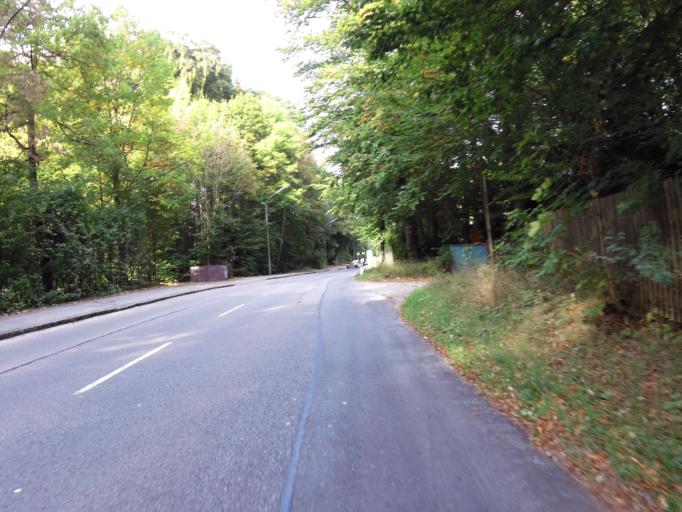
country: DE
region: Bavaria
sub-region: Upper Bavaria
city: Berg
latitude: 47.9781
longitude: 11.3290
